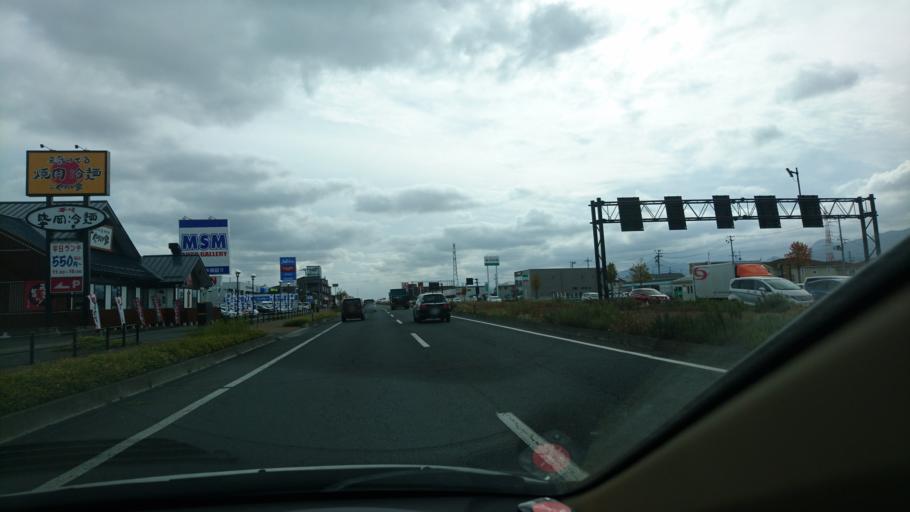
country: JP
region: Iwate
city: Morioka-shi
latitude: 39.6844
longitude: 141.1357
